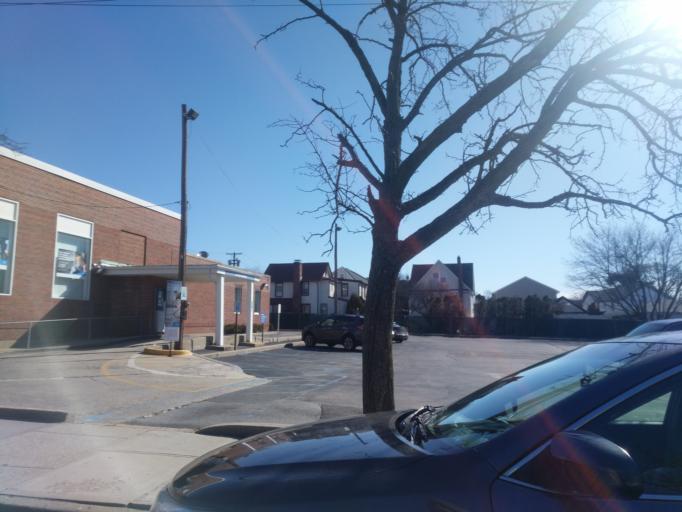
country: US
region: New York
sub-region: Nassau County
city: Inwood
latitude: 40.6152
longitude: -73.7466
